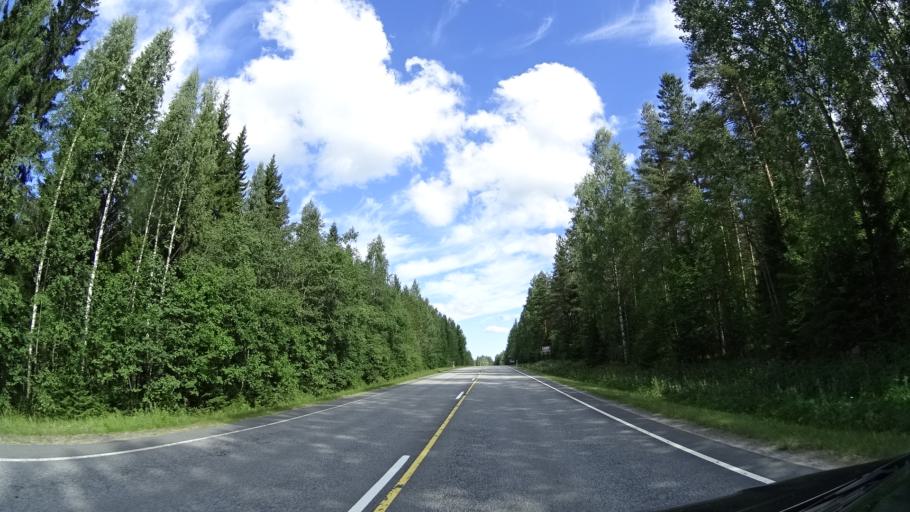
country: FI
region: Pirkanmaa
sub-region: Luoteis-Pirkanmaa
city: Kihnioe
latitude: 62.1862
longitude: 23.1724
